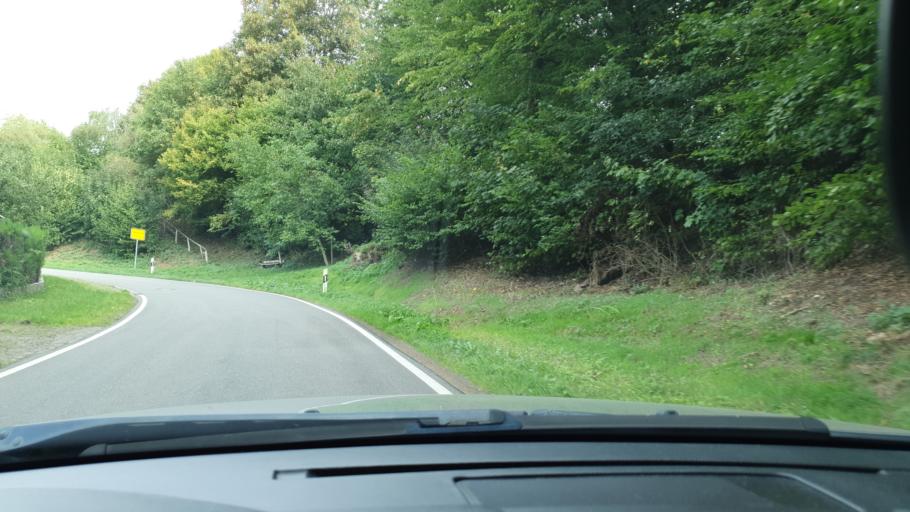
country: DE
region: Rheinland-Pfalz
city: Grossbundenbach
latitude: 49.3047
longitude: 7.4217
